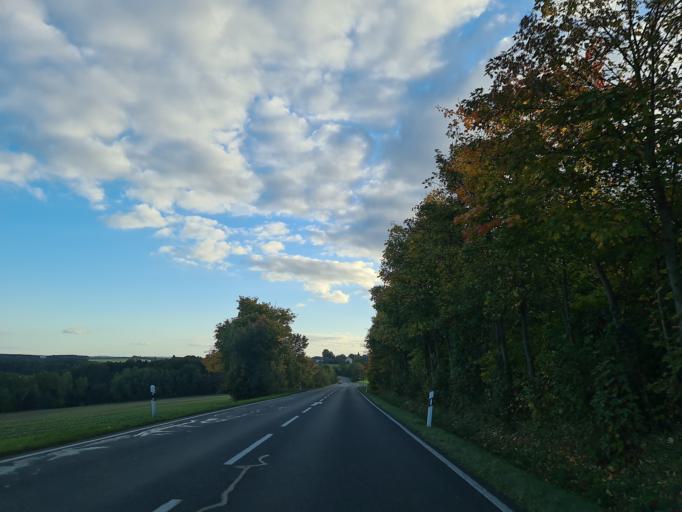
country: DE
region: Thuringia
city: Teichwitz
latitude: 50.7468
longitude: 12.0886
